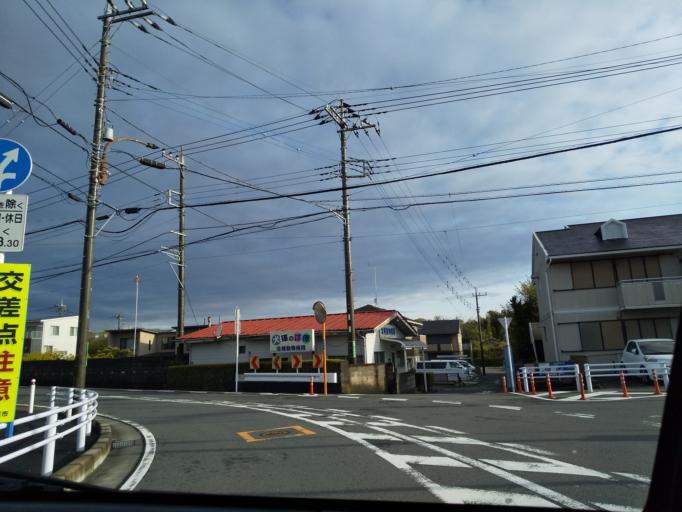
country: JP
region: Tokyo
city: Hachioji
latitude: 35.6018
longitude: 139.3290
